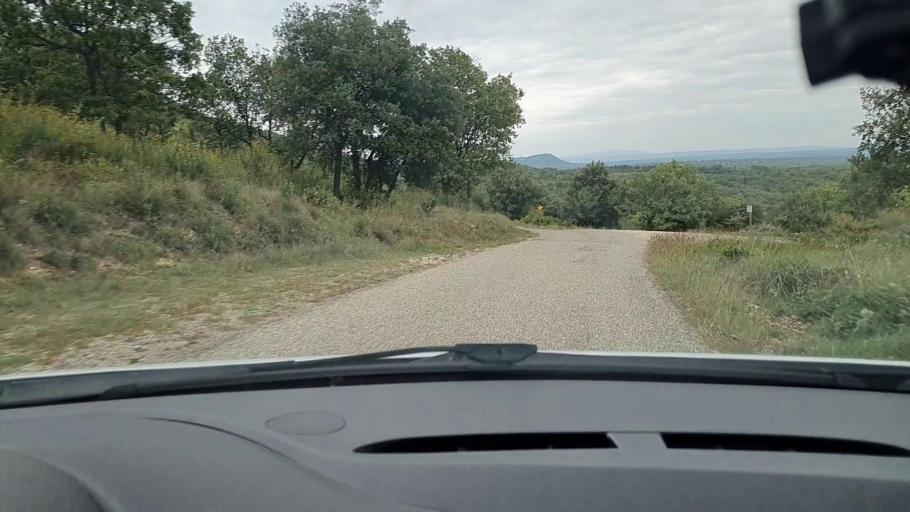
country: FR
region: Languedoc-Roussillon
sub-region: Departement du Gard
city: Mons
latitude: 44.1334
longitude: 4.2899
